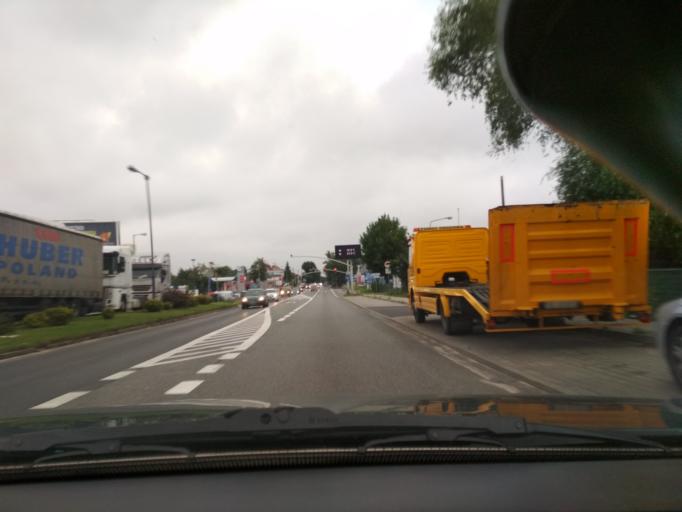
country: PL
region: Silesian Voivodeship
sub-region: Gliwice
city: Gliwice
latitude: 50.2750
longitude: 18.6615
